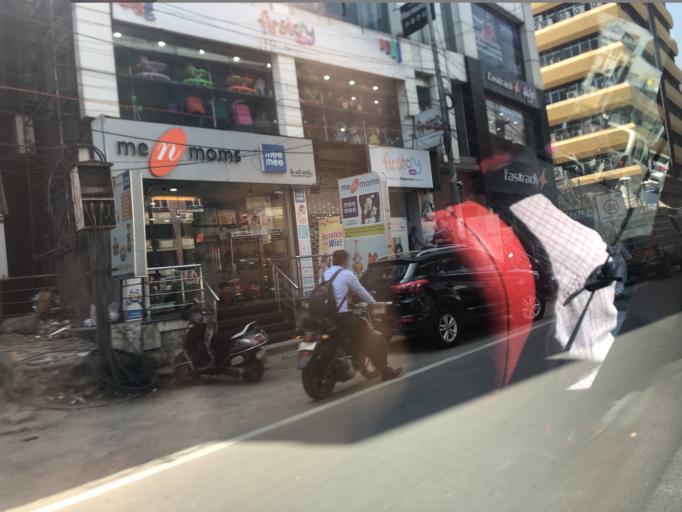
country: IN
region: Telangana
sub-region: Rangareddi
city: Quthbullapur
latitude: 17.4446
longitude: 78.4635
